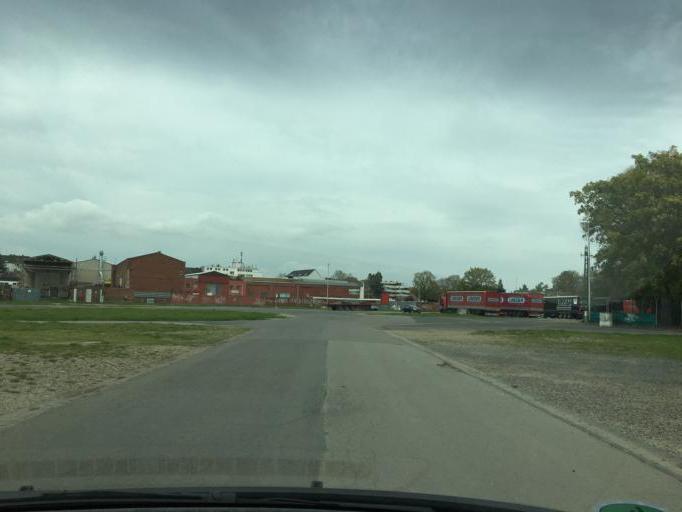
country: DE
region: North Rhine-Westphalia
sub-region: Regierungsbezirk Koln
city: Dueren
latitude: 50.7940
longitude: 6.4787
